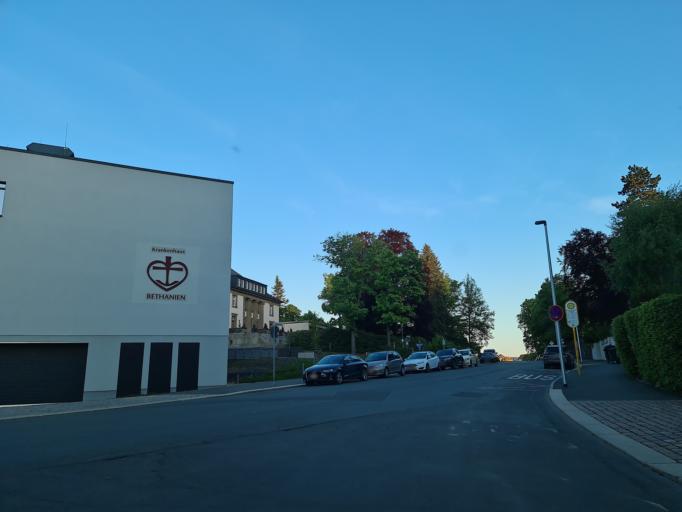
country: DE
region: Saxony
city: Plauen
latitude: 50.5023
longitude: 12.1219
